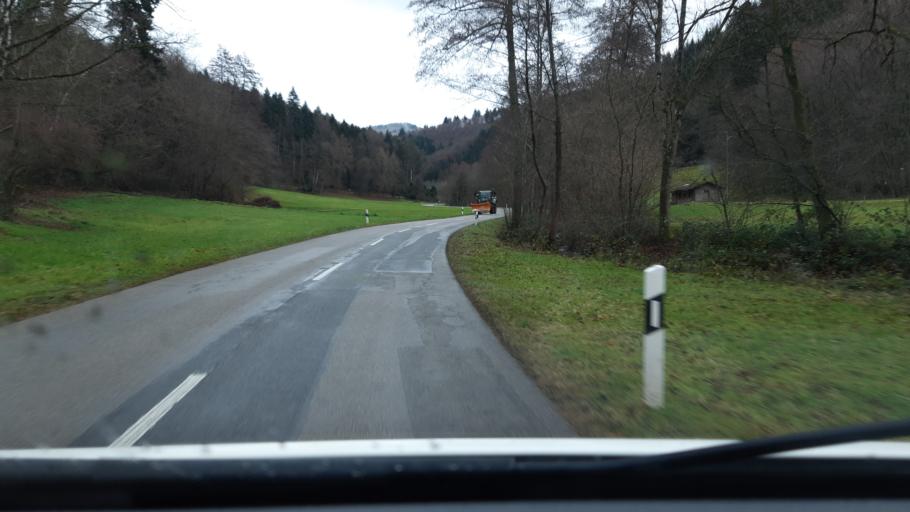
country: DE
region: Baden-Wuerttemberg
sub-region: Freiburg Region
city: Solden
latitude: 47.9192
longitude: 7.8084
